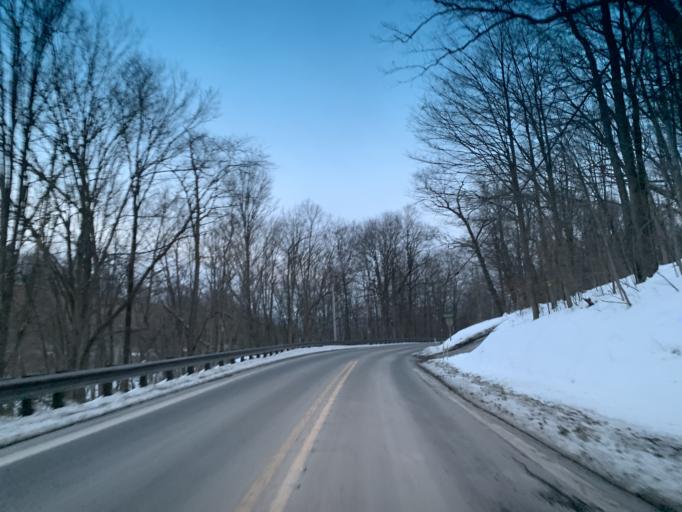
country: US
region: Maryland
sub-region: Allegany County
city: Cumberland
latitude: 39.6959
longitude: -78.5160
